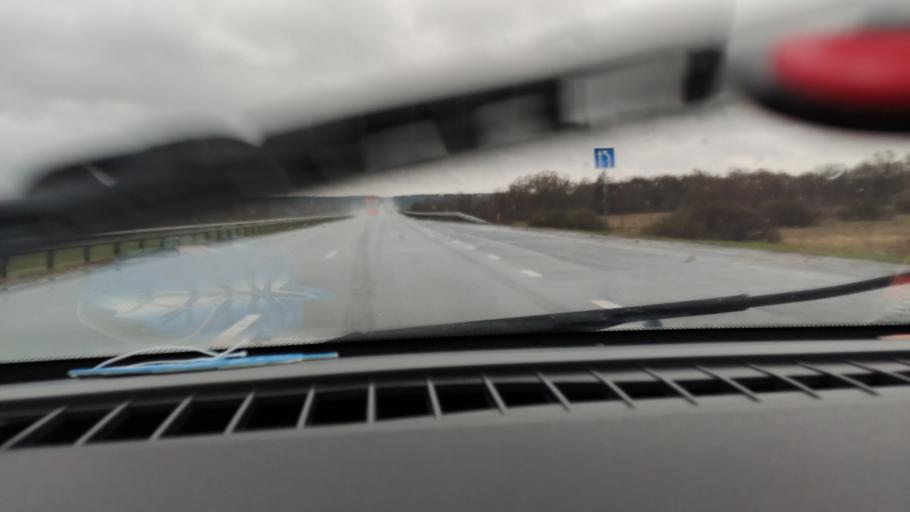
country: RU
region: Tatarstan
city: Yelabuga
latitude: 55.7700
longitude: 52.2141
